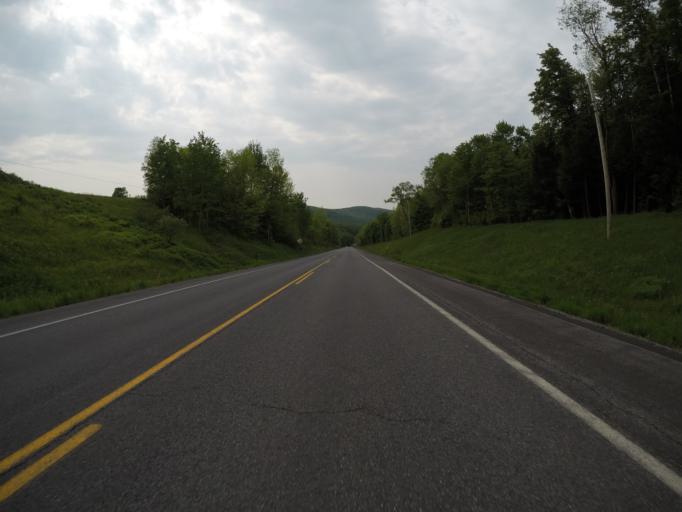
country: US
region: New York
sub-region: Sullivan County
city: Livingston Manor
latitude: 42.0288
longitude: -74.8951
